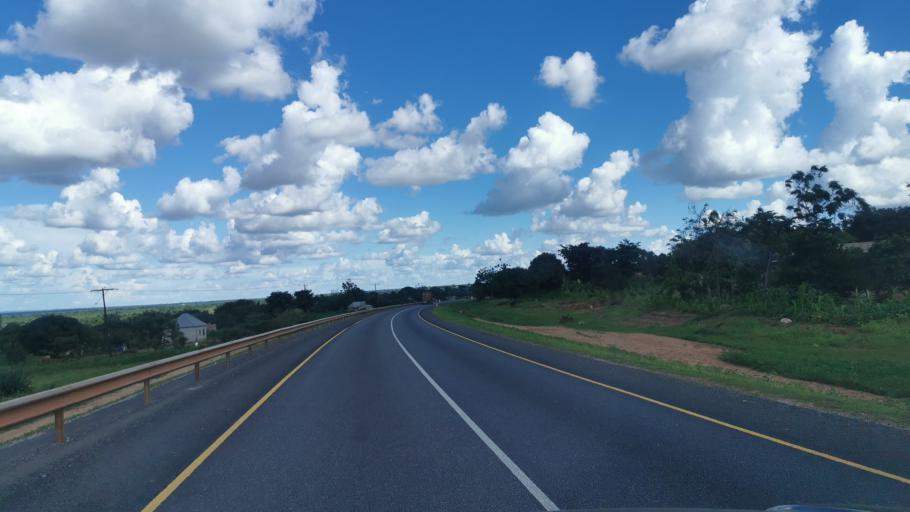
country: TZ
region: Geita
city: Ushirombo
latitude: -3.4350
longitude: 31.8316
